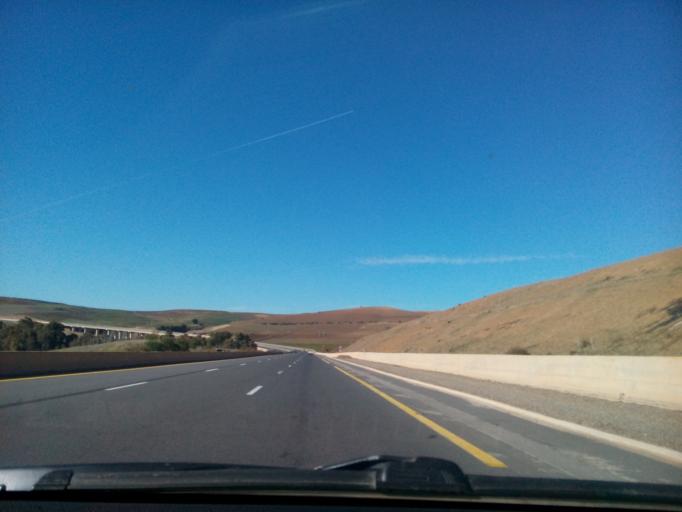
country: DZ
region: Tlemcen
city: Sidi Abdelli
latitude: 35.0392
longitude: -1.0591
